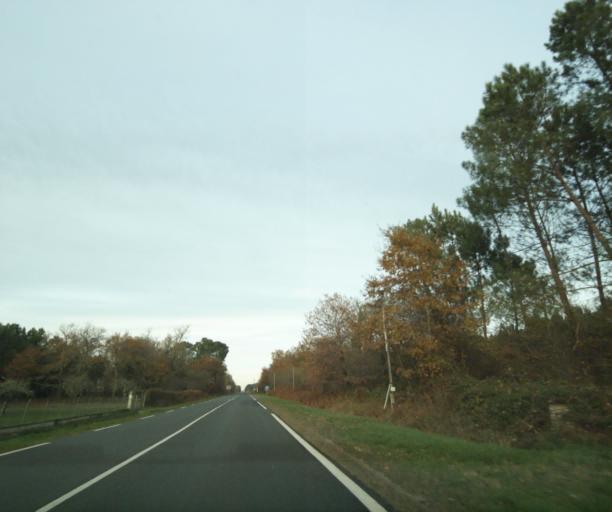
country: FR
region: Aquitaine
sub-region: Departement de la Gironde
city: Bazas
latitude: 44.3123
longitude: -0.2489
